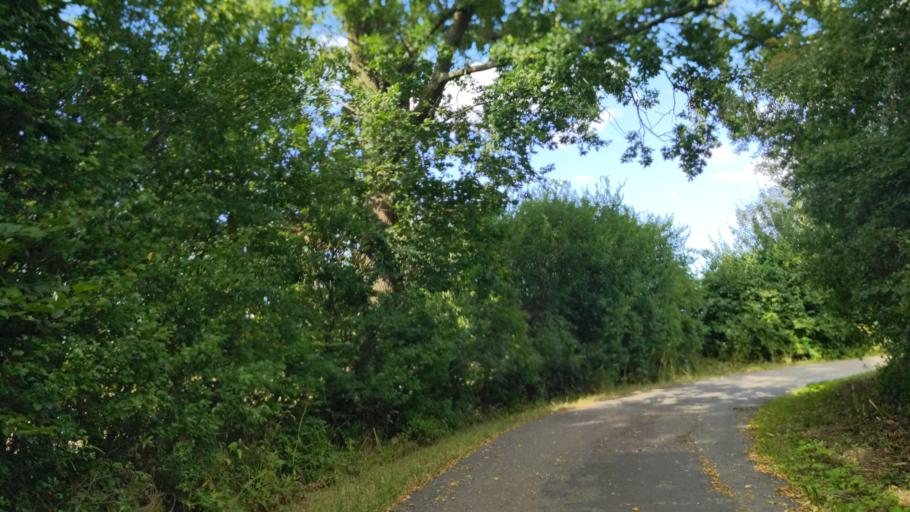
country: DE
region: Schleswig-Holstein
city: Stockelsdorf
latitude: 53.9520
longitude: 10.6145
